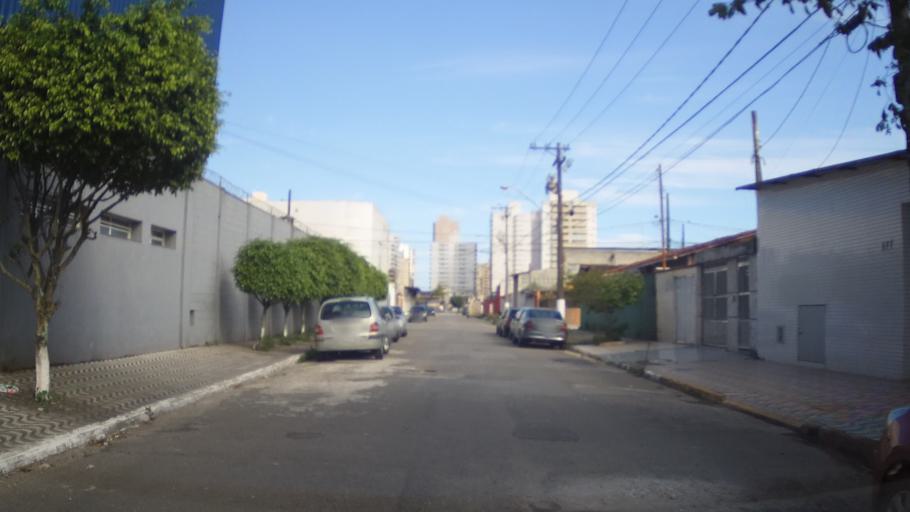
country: BR
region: Sao Paulo
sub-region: Praia Grande
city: Praia Grande
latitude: -24.0139
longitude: -46.4518
